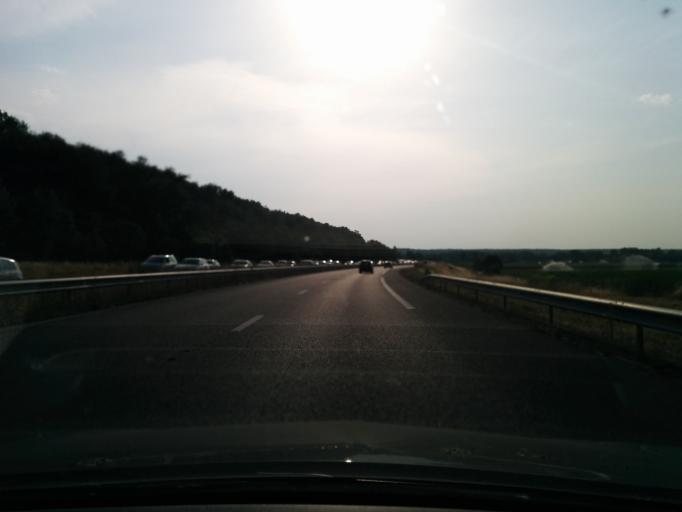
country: FR
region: Midi-Pyrenees
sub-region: Departement de la Haute-Garonne
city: Buzet-sur-Tarn
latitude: 43.7467
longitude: 1.6296
